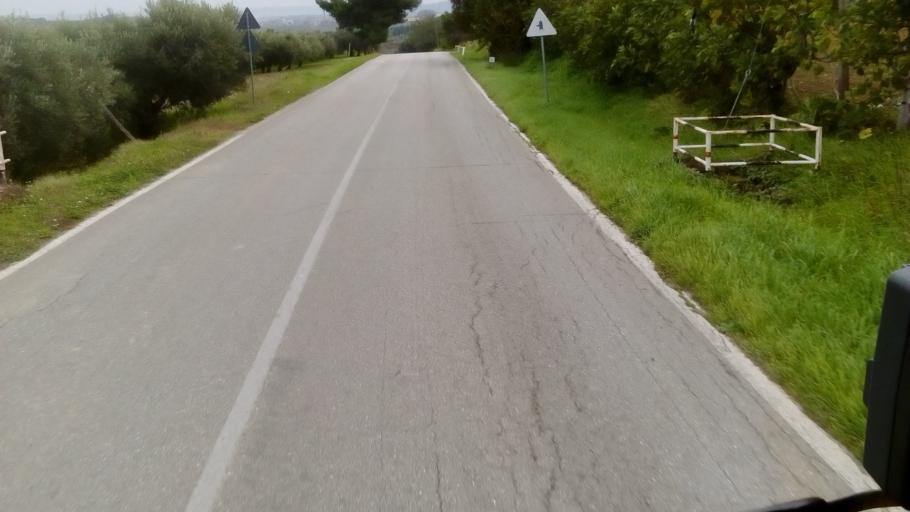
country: IT
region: Abruzzo
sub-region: Provincia di Chieti
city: Cupello
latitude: 42.0581
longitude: 14.7001
